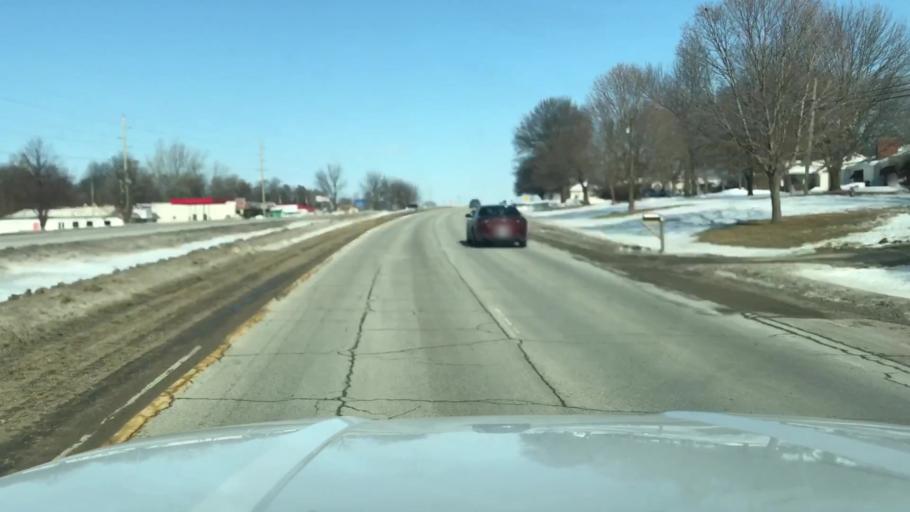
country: US
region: Missouri
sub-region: Andrew County
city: Savannah
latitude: 39.9354
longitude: -94.8217
